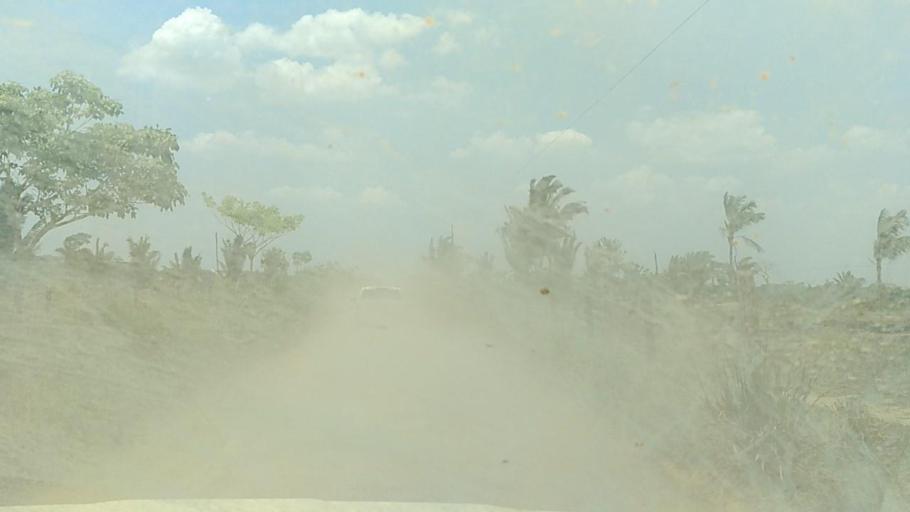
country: BR
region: Rondonia
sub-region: Porto Velho
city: Porto Velho
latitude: -8.7294
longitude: -63.3067
